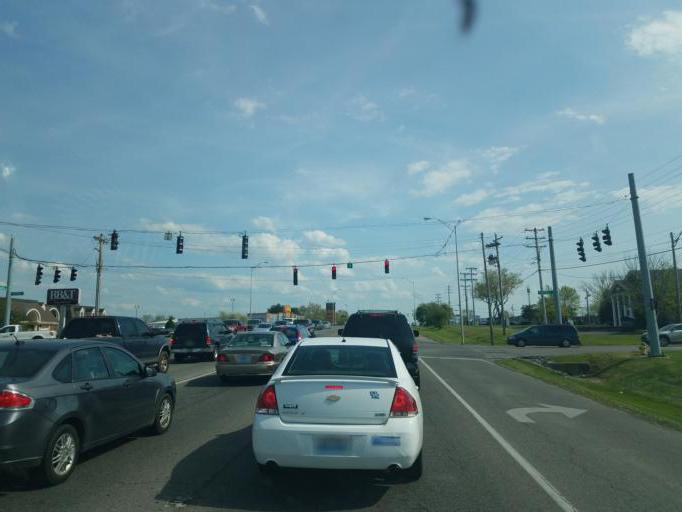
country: US
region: Kentucky
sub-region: Warren County
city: Bowling Green
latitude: 36.9665
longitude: -86.4324
